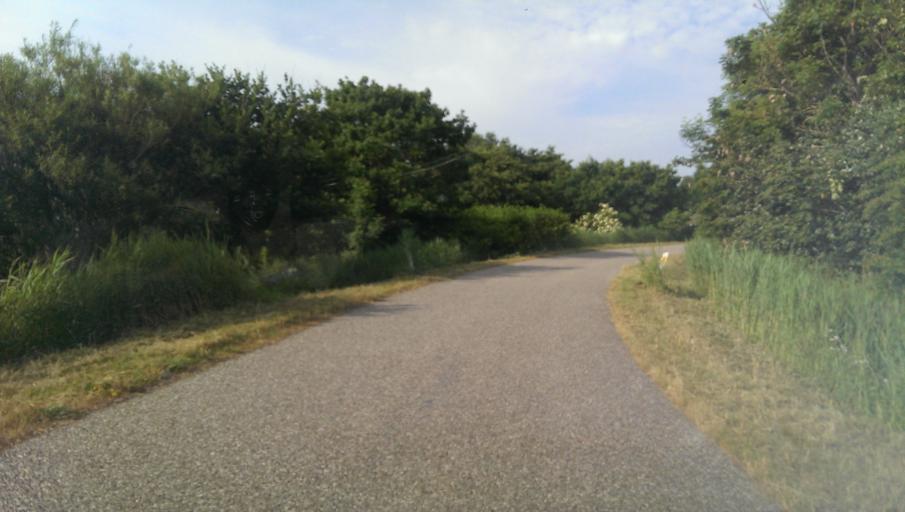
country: DK
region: South Denmark
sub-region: Esbjerg Kommune
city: Tjaereborg
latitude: 55.4347
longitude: 8.6121
